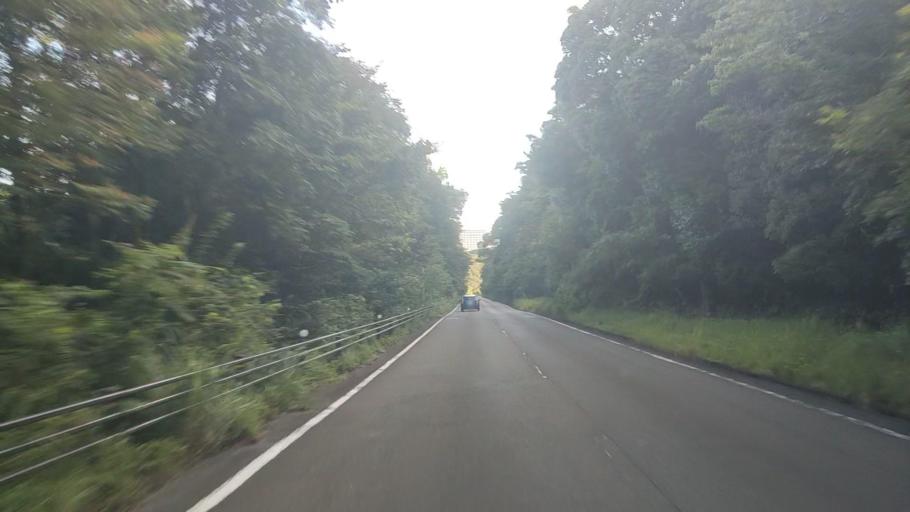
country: JP
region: Mie
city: Toba
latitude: 34.3789
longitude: 136.8556
